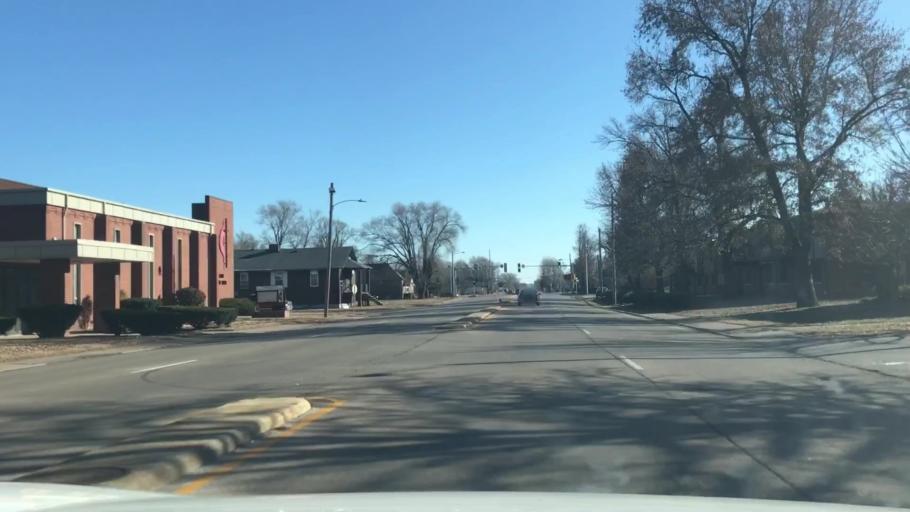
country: US
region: Illinois
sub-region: Saint Clair County
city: East Saint Louis
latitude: 38.6178
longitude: -90.1490
